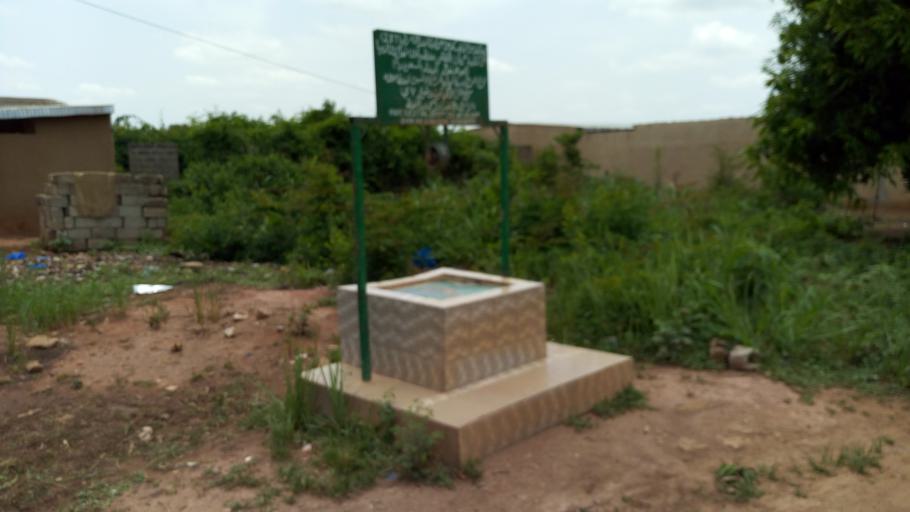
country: CI
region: Vallee du Bandama
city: Bouake
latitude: 7.7288
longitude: -4.9955
